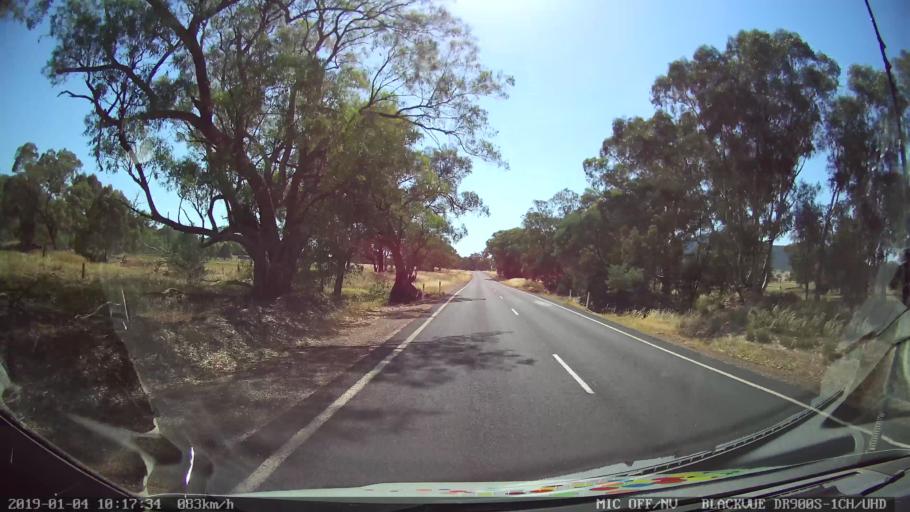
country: AU
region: New South Wales
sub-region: Cabonne
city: Canowindra
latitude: -33.3839
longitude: 148.4534
